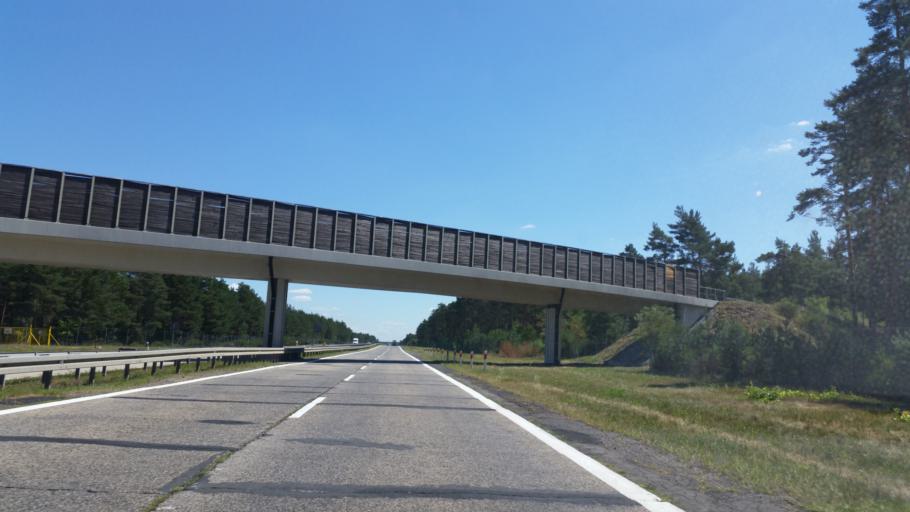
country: PL
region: Lubusz
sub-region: Powiat zaganski
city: Malomice
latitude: 51.4298
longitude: 15.4159
